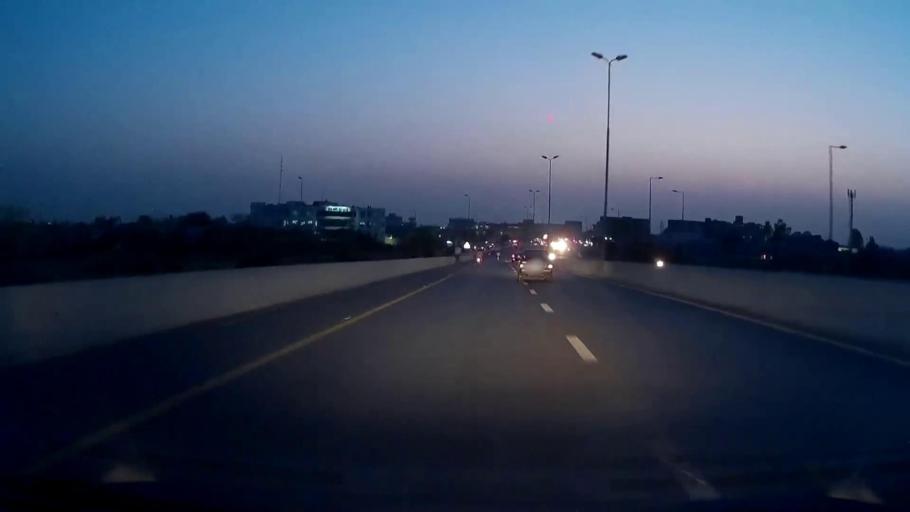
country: PK
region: Punjab
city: Lahore
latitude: 31.4985
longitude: 74.4246
